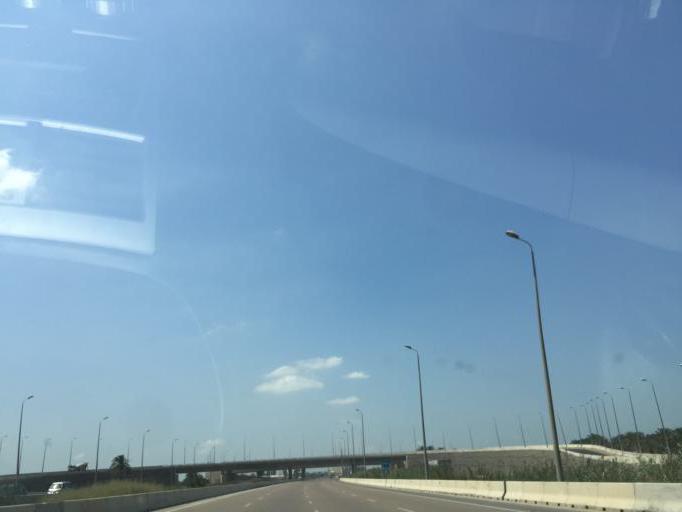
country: EG
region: Al Buhayrah
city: Abu al Matamir
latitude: 30.8864
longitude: 29.8812
